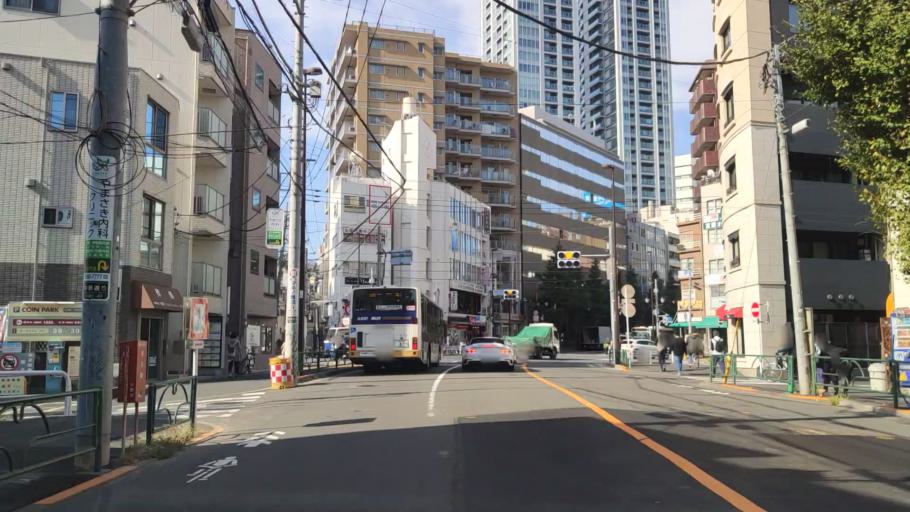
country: JP
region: Tokyo
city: Tokyo
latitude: 35.7023
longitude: 139.6660
